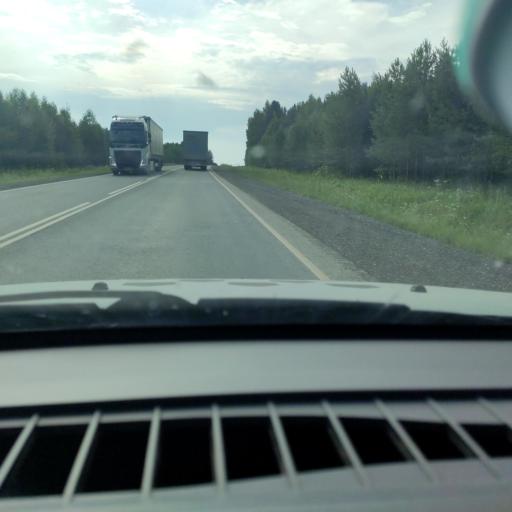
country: RU
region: Perm
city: Siva
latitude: 58.4287
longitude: 54.4478
